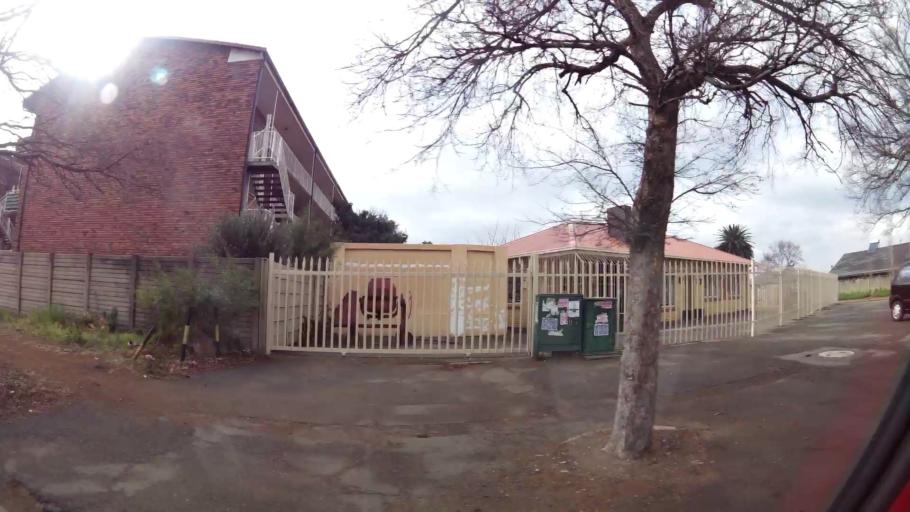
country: ZA
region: Gauteng
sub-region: Sedibeng District Municipality
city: Vanderbijlpark
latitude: -26.6940
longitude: 27.8403
